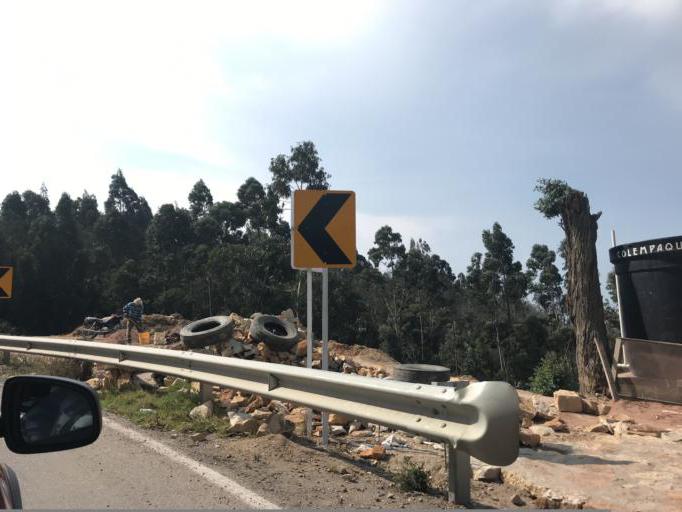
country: CO
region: Boyaca
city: Samaca
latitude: 5.4871
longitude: -73.4793
